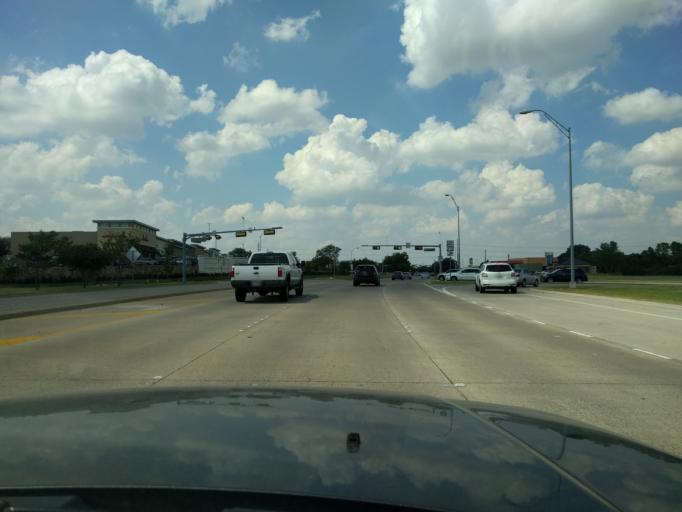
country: US
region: Texas
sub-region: Collin County
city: Allen
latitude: 33.0664
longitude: -96.6910
